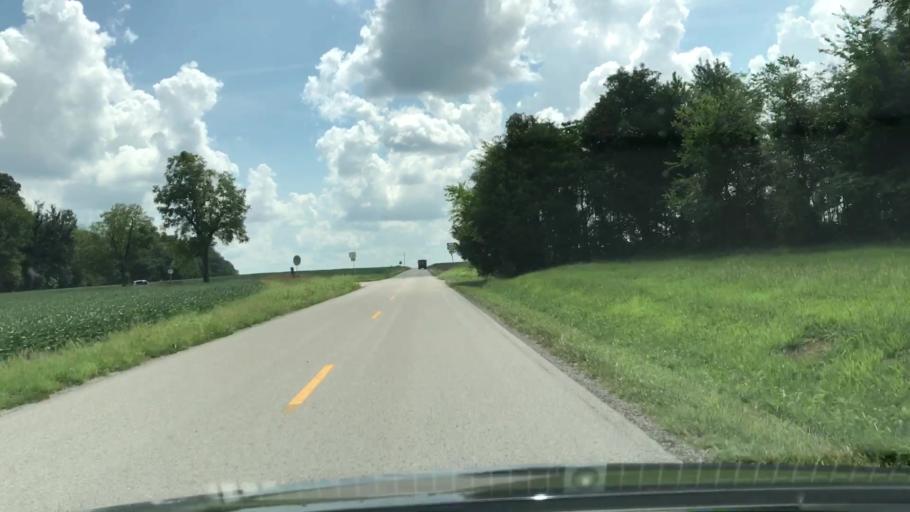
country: US
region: Kentucky
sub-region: Todd County
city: Guthrie
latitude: 36.7008
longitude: -87.0409
